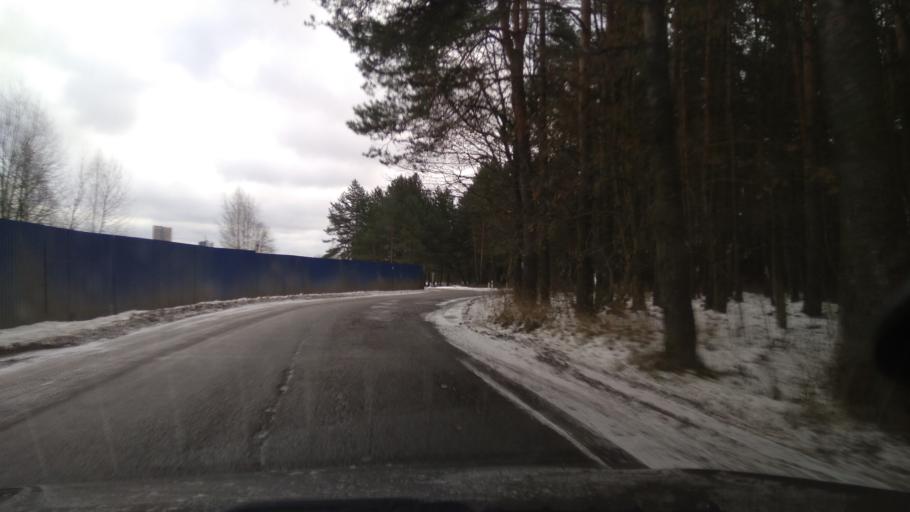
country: BY
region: Minsk
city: Borovlyany
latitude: 53.9643
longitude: 27.6462
